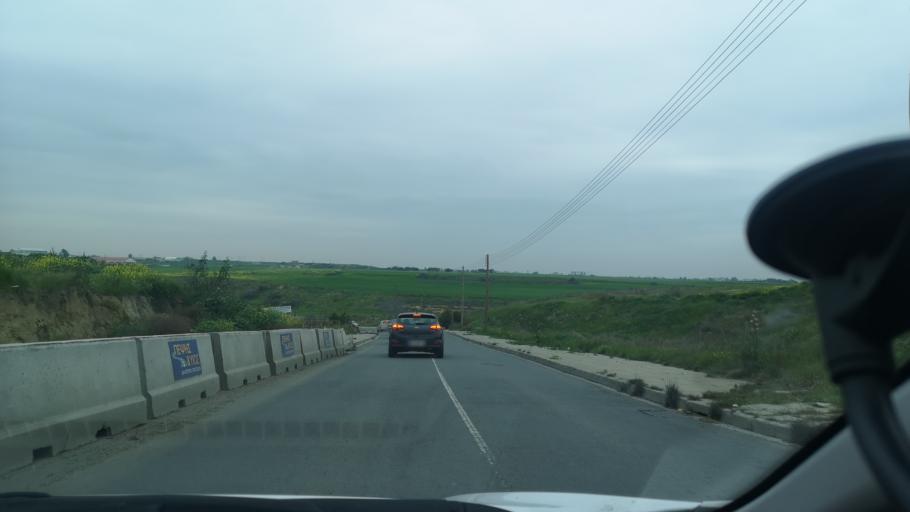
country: CY
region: Lefkosia
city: Tseri
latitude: 35.1021
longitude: 33.3467
